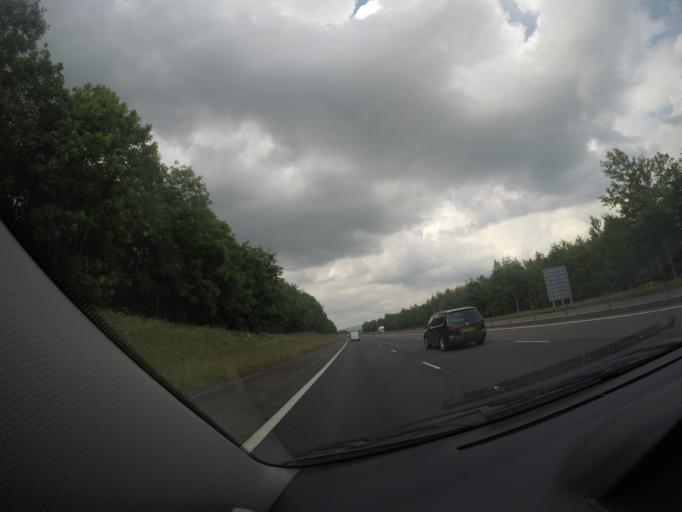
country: GB
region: Scotland
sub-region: Dumfries and Galloway
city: Moffat
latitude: 55.2490
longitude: -3.4098
